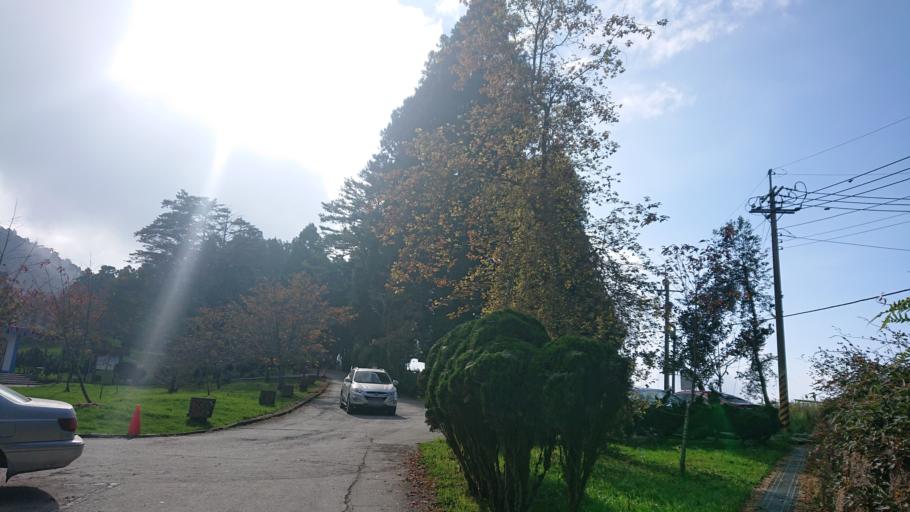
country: TW
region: Taiwan
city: Lugu
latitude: 23.5091
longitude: 120.7909
